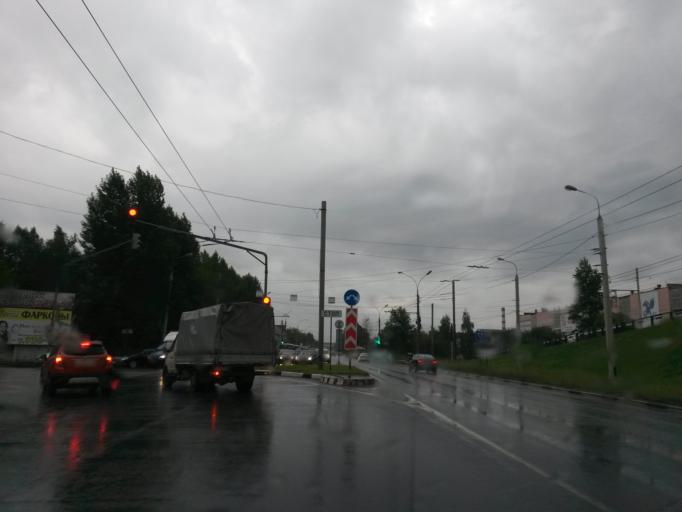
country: RU
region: Jaroslavl
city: Yaroslavl
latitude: 57.6629
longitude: 39.8432
